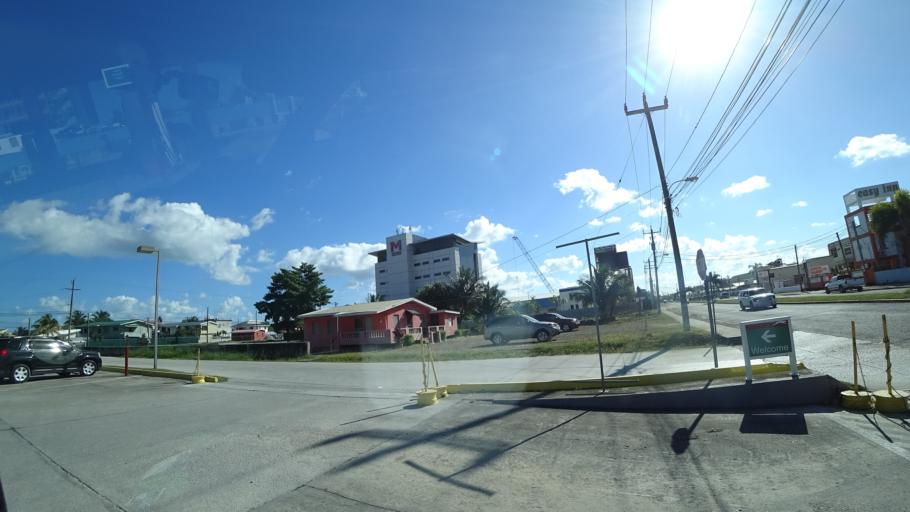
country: BZ
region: Belize
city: Belize City
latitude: 17.5084
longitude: -88.2057
